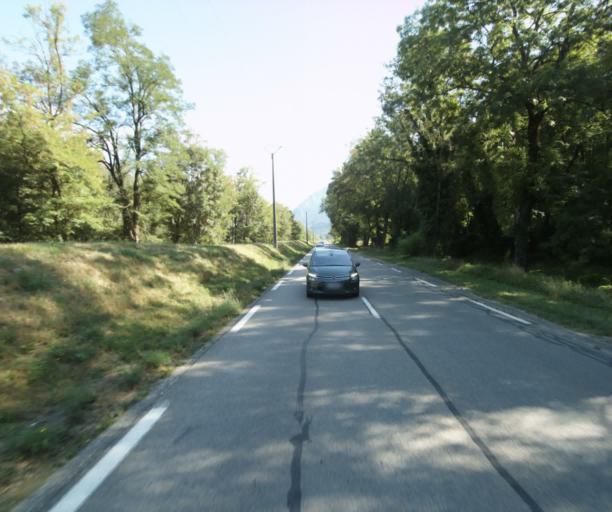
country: FR
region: Rhone-Alpes
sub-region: Departement de l'Isere
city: Veurey-Voroize
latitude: 45.2834
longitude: 5.6171
